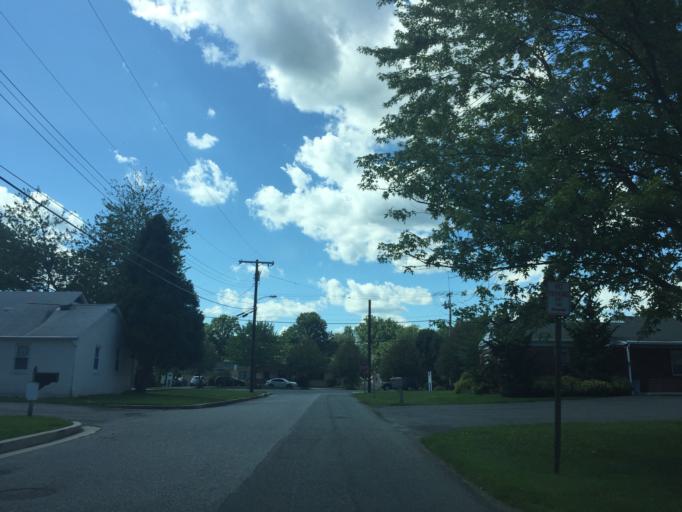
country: US
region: Maryland
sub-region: Baltimore County
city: Perry Hall
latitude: 39.4050
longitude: -76.4717
